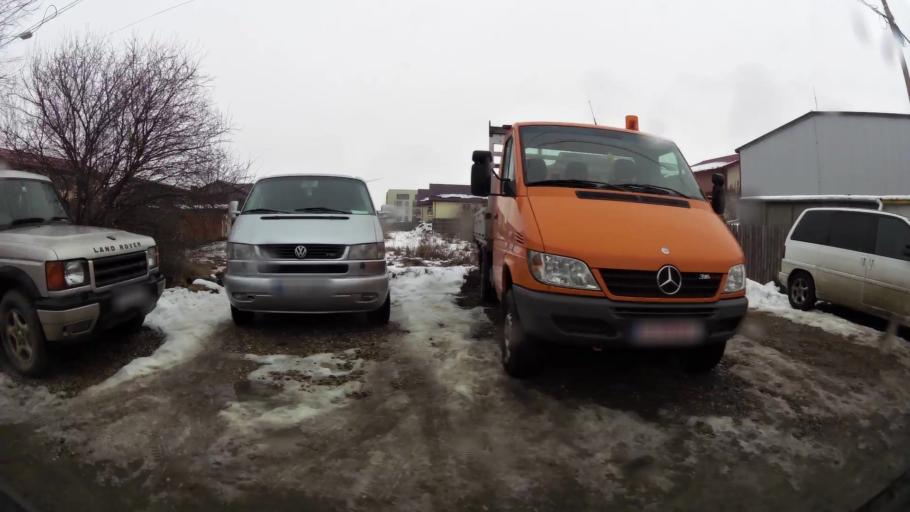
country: RO
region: Ilfov
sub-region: Comuna Glina
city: Catelu
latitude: 44.4137
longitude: 26.1886
